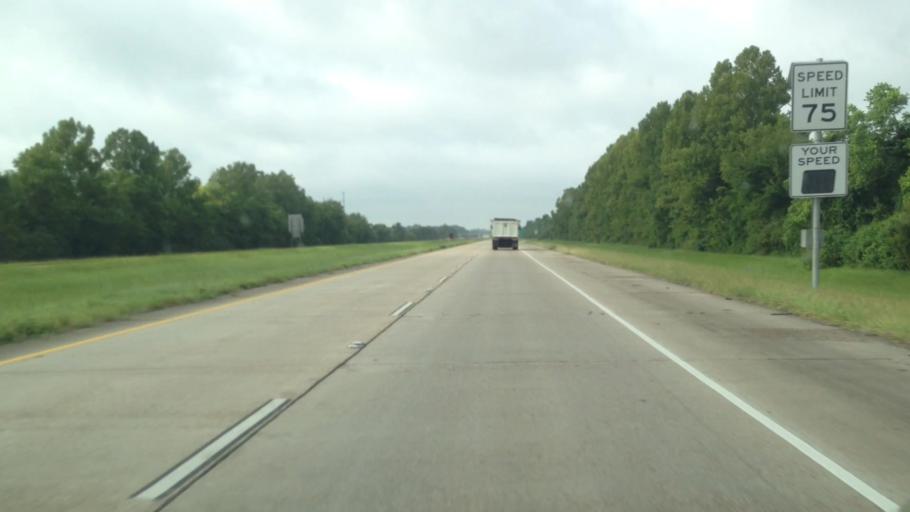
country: US
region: Louisiana
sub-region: Saint Landry Parish
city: Opelousas
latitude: 30.6330
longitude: -92.0481
